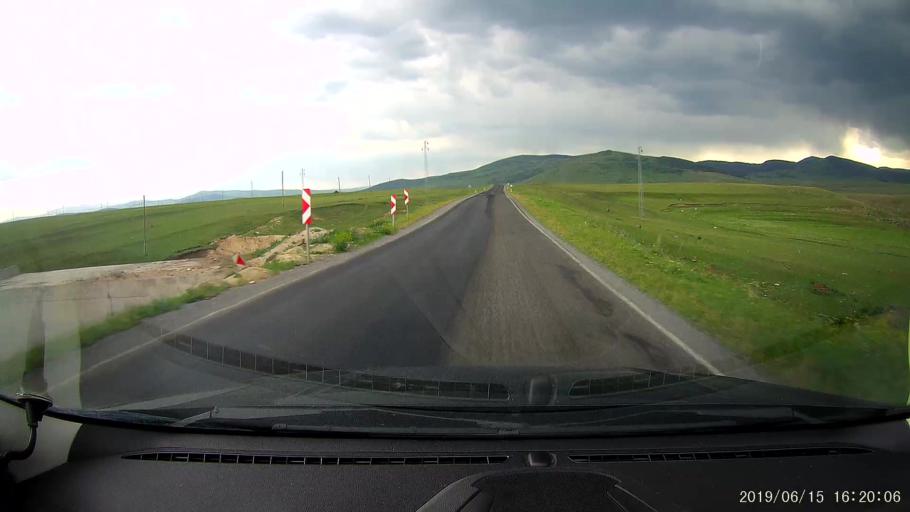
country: TR
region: Ardahan
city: Hanak
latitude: 41.2197
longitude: 42.8496
